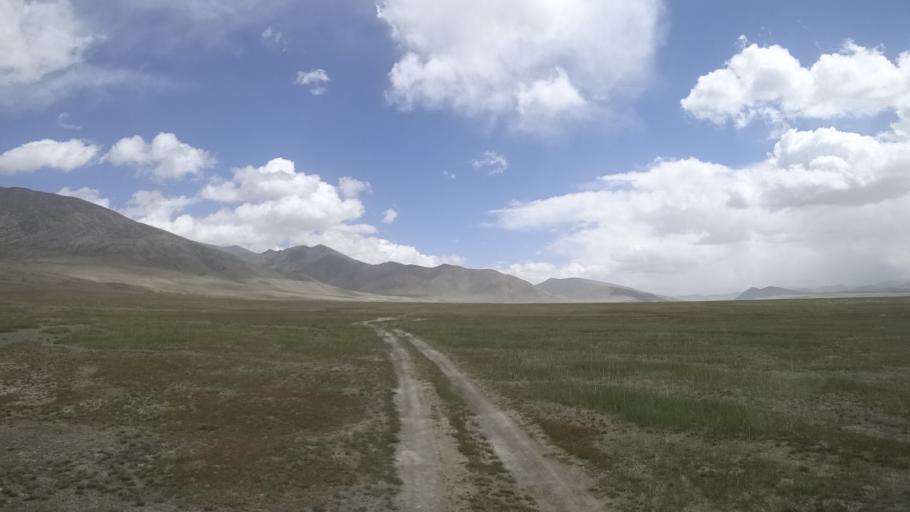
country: TJ
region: Gorno-Badakhshan
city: Murghob
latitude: 37.4834
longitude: 73.9839
